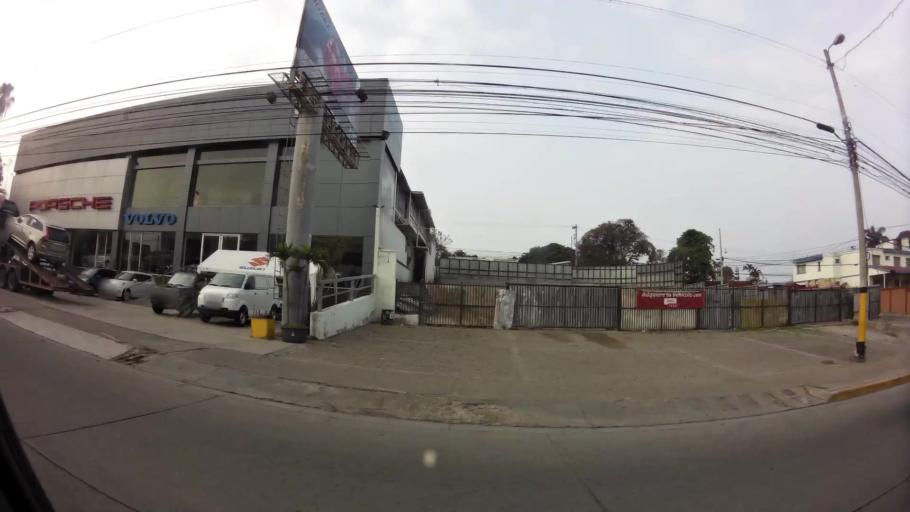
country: HN
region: Francisco Morazan
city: Tegucigalpa
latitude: 14.0842
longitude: -87.1803
